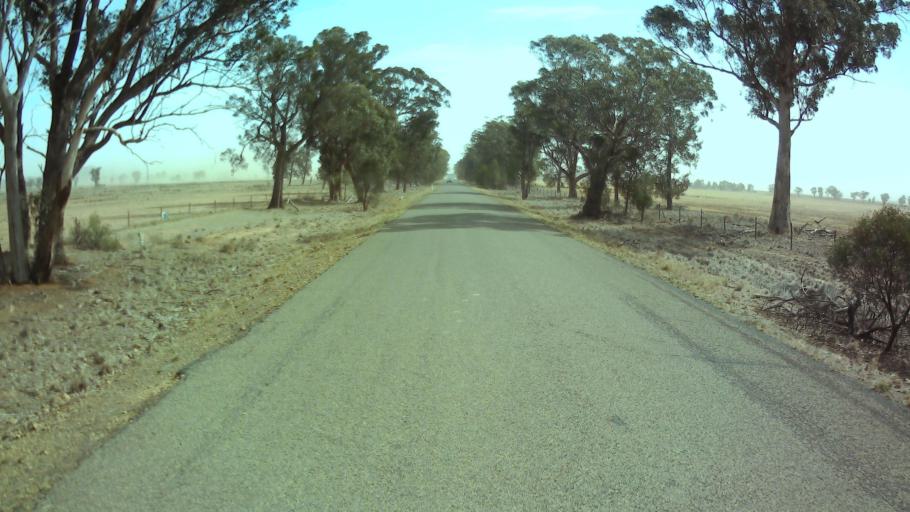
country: AU
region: New South Wales
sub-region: Weddin
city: Grenfell
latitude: -33.7589
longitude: 147.9892
